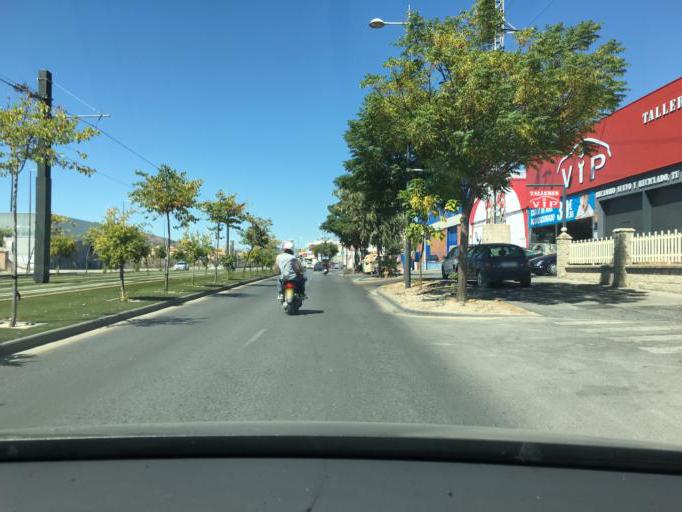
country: ES
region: Andalusia
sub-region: Provincia de Granada
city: Albolote
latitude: 37.2215
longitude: -3.6447
